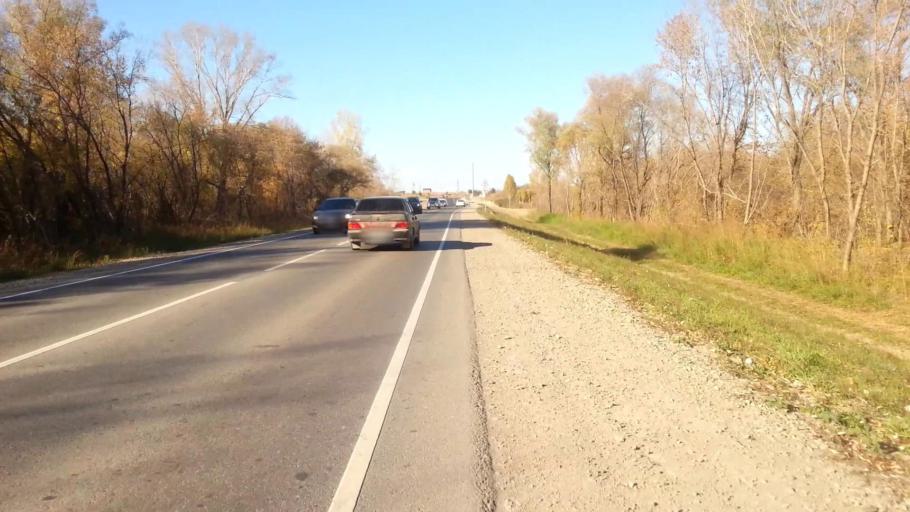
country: RU
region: Altai Krai
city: Sannikovo
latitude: 53.3248
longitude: 83.9425
